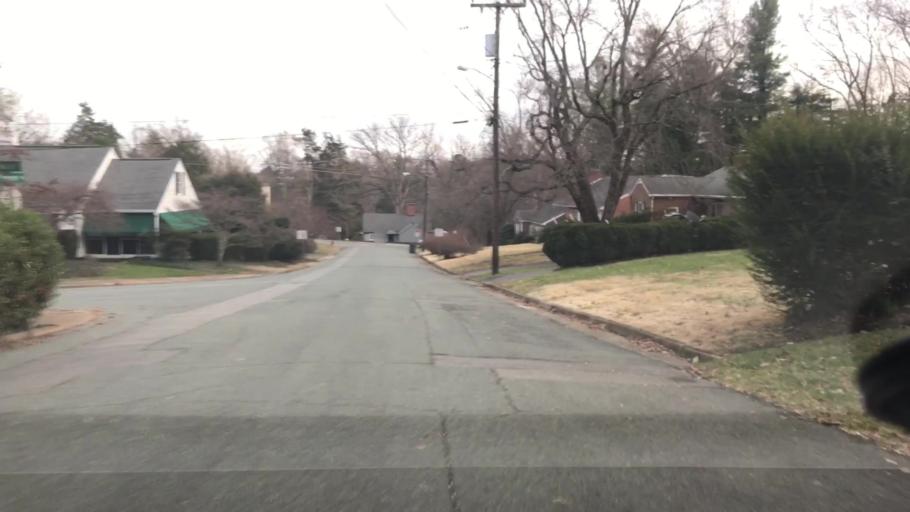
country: US
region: Virginia
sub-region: City of Charlottesville
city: Charlottesville
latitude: 38.0417
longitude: -78.5145
